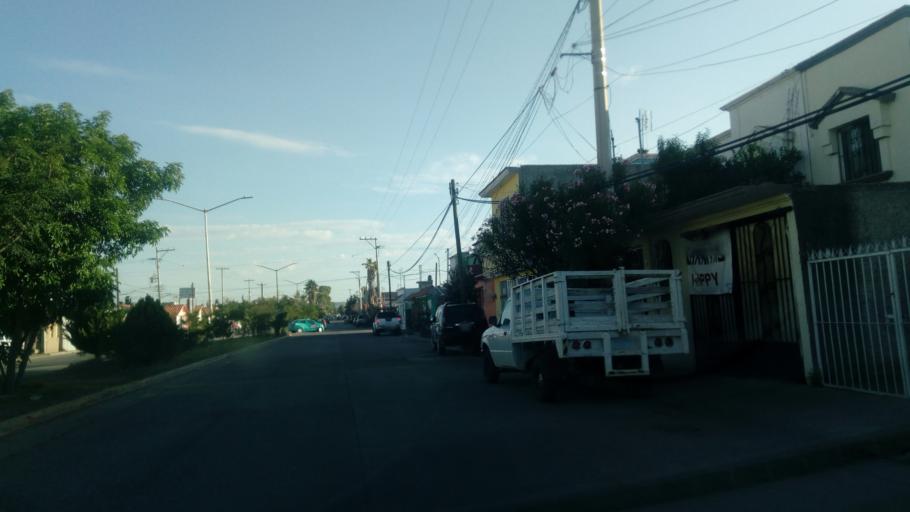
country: MX
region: Durango
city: Victoria de Durango
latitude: 24.0696
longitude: -104.5867
